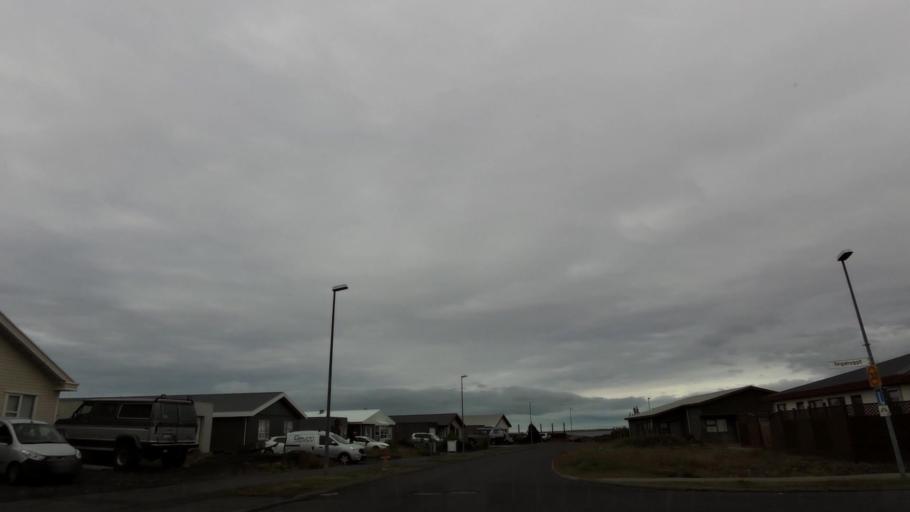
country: IS
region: Capital Region
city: Alftanes
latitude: 64.0556
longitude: -21.9927
